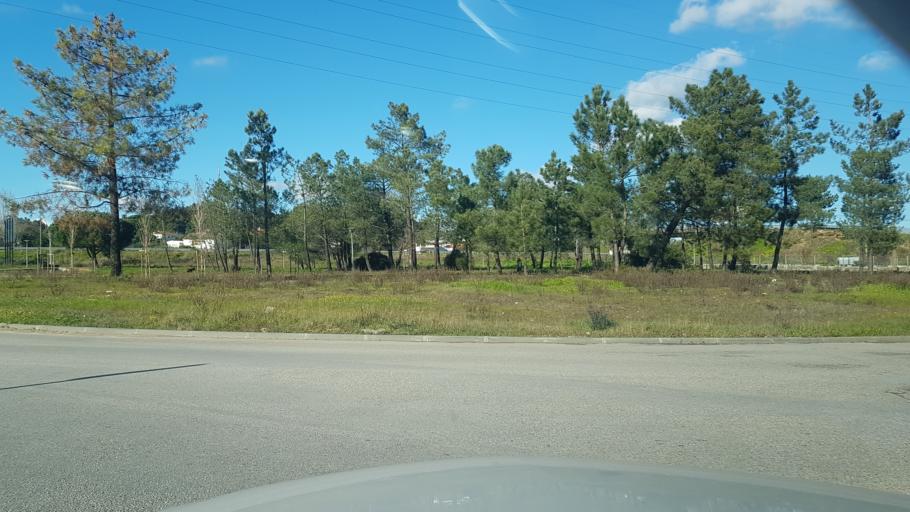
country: PT
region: Santarem
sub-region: Entroncamento
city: Entroncamento
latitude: 39.4767
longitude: -8.4825
